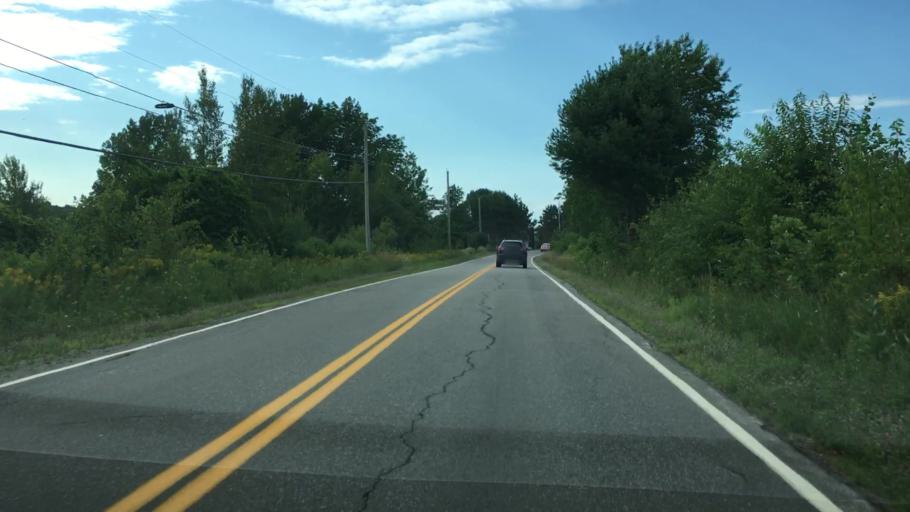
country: US
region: Maine
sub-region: Waldo County
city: Belfast
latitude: 44.3774
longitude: -69.0329
